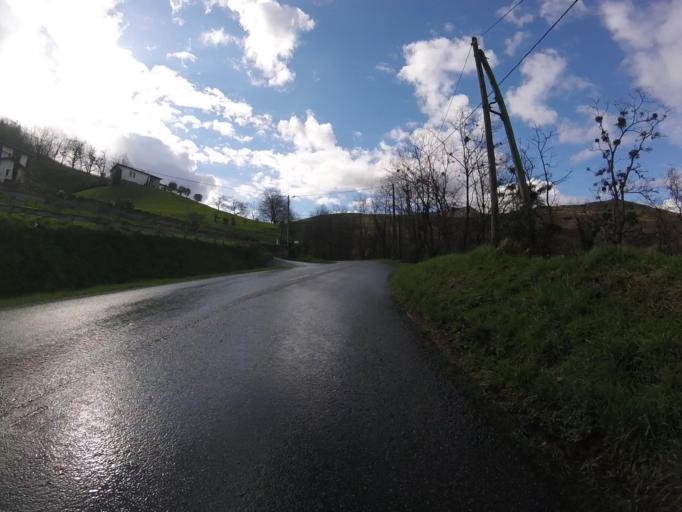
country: FR
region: Aquitaine
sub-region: Departement des Pyrenees-Atlantiques
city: Ascain
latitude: 43.3384
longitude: -1.6157
